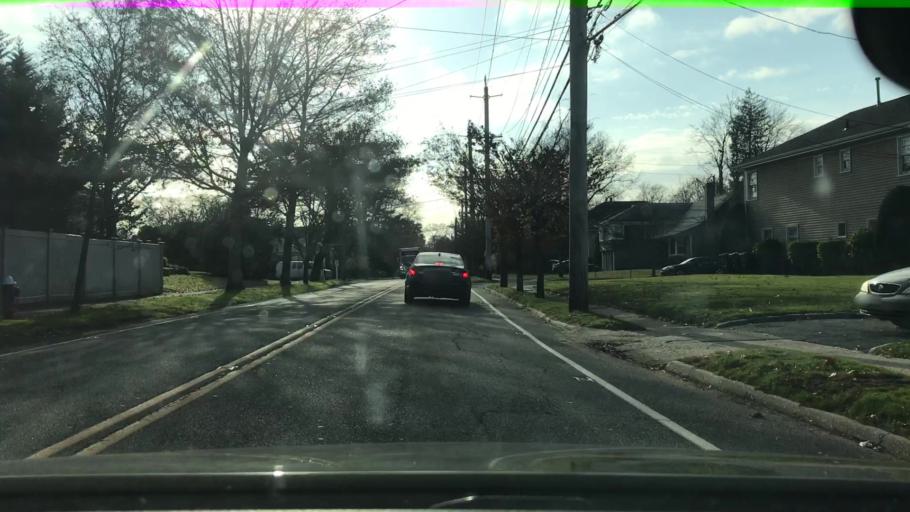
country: US
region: New York
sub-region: Nassau County
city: Cedarhurst
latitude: 40.6214
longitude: -73.7189
